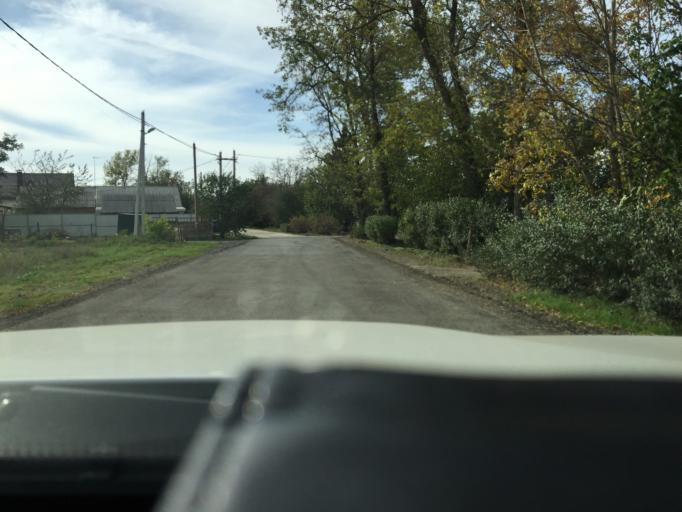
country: RU
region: Rostov
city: Aksay
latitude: 47.3027
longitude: 39.8313
